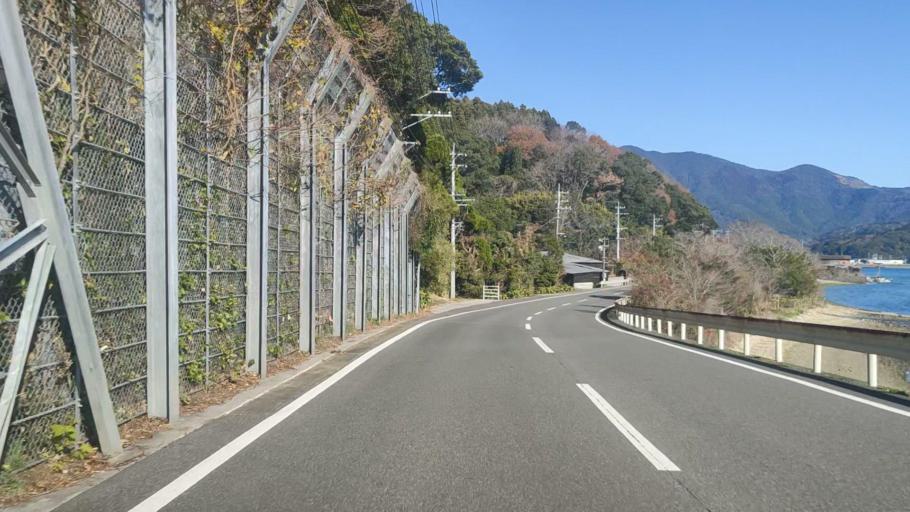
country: JP
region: Oita
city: Saiki
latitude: 32.7974
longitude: 131.8865
